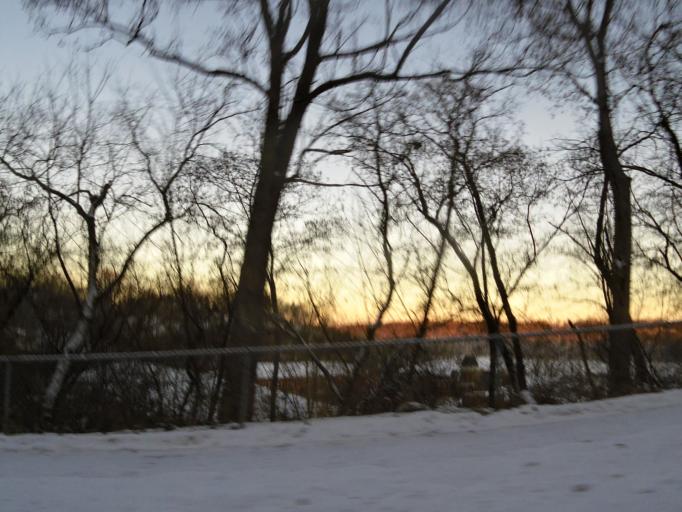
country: US
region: Minnesota
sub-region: Washington County
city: Stillwater
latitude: 45.0621
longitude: -92.8100
